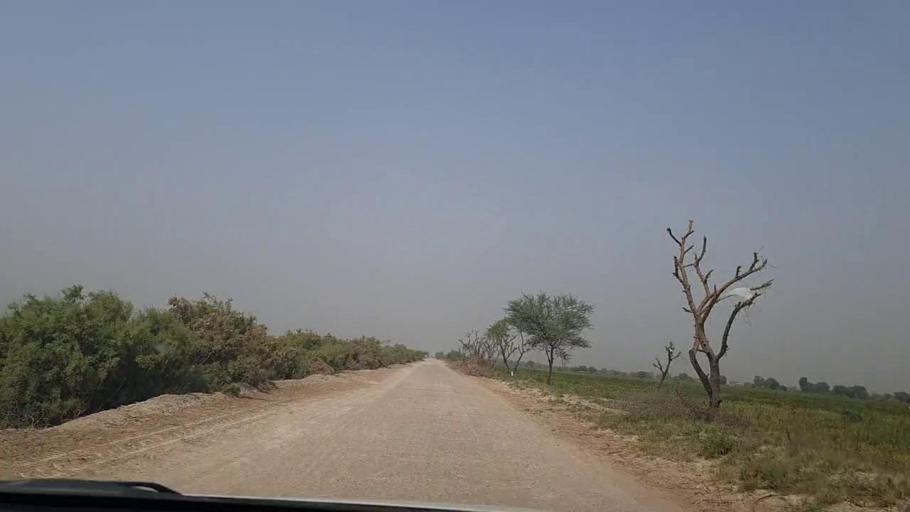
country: PK
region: Sindh
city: Mirpur Khas
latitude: 25.5898
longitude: 69.2010
